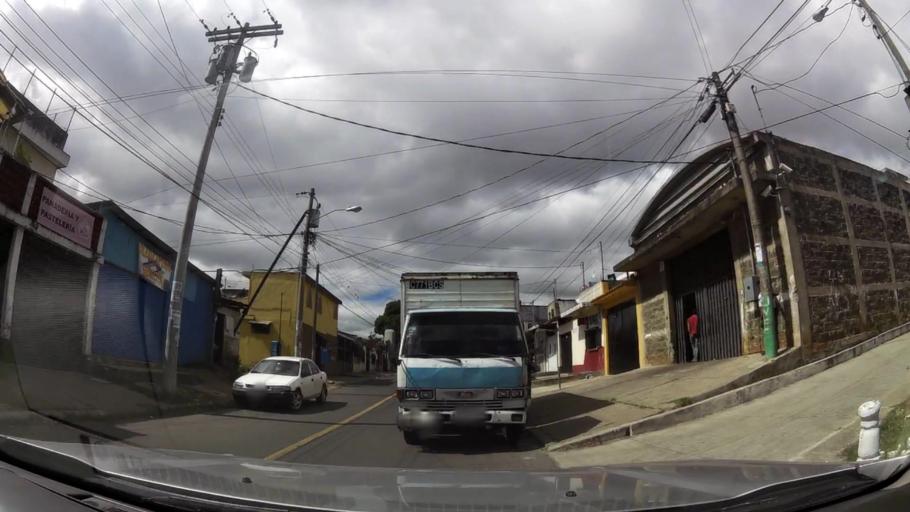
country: GT
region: Guatemala
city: Guatemala City
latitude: 14.6388
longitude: -90.5579
